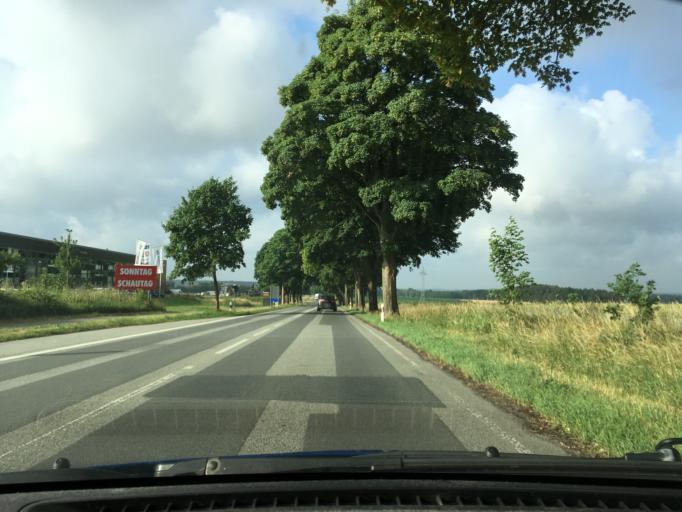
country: DE
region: Lower Saxony
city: Kakenstorf
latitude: 53.3247
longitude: 9.8110
